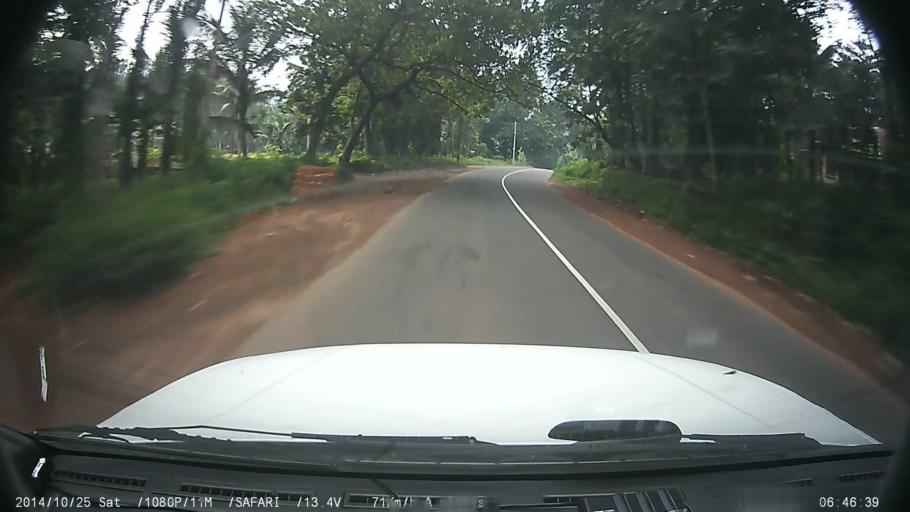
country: IN
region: Kerala
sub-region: Ernakulam
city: Muvattupuzha
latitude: 9.9382
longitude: 76.5766
